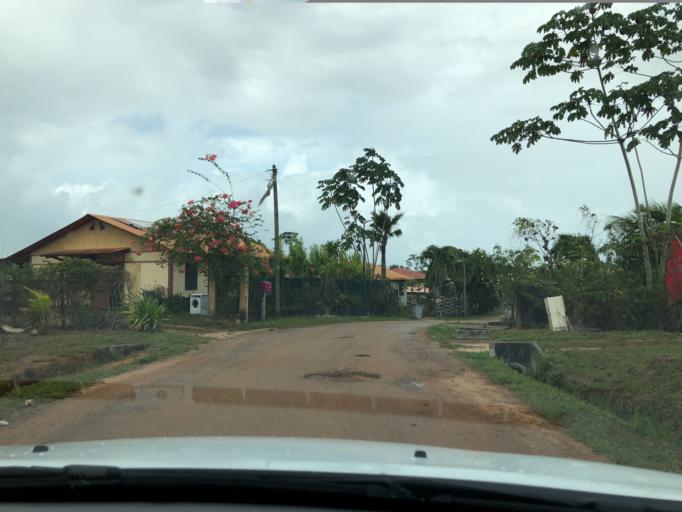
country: GF
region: Guyane
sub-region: Guyane
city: Mana
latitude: 5.6060
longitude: -53.8214
